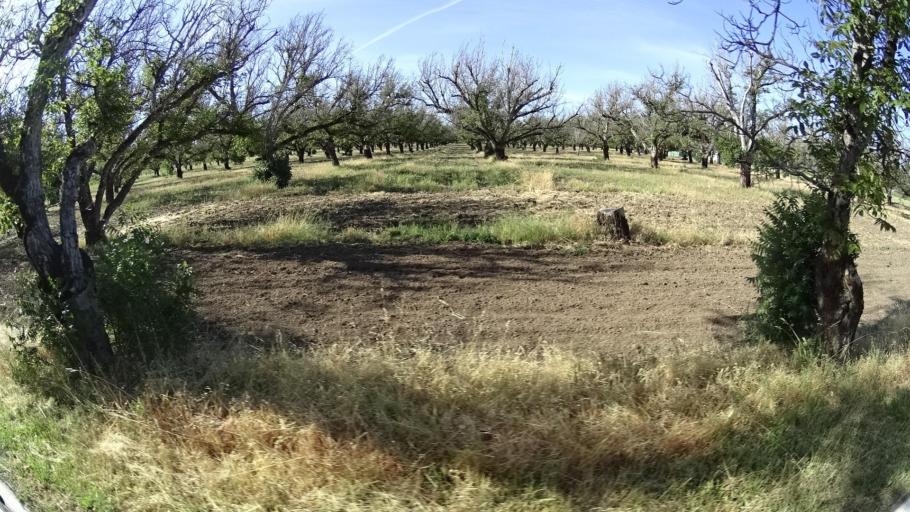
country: US
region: California
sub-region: Lake County
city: Lakeport
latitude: 39.0149
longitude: -122.8767
